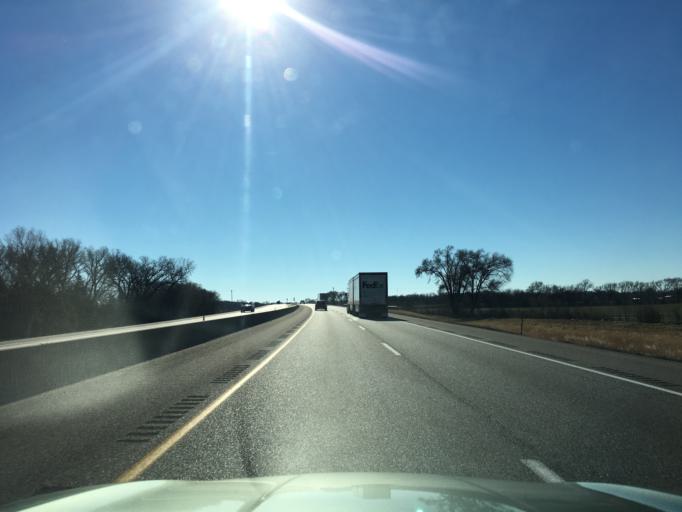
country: US
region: Kansas
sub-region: Sumner County
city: Belle Plaine
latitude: 37.3961
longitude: -97.3261
